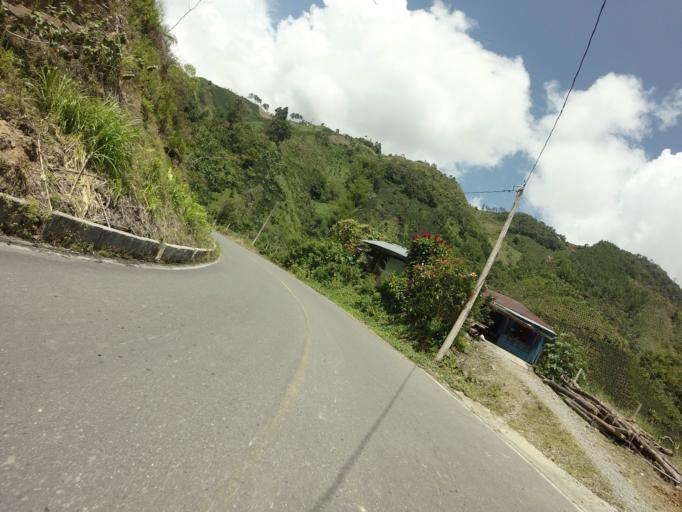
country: CO
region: Caldas
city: Marquetalia
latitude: 5.2918
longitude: -75.1052
